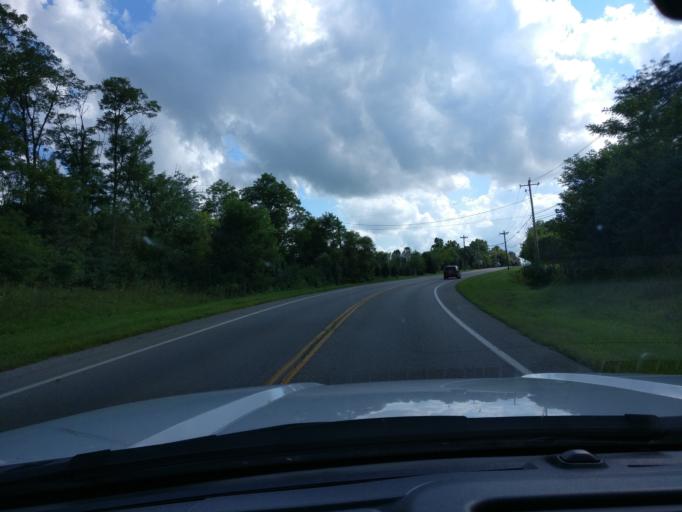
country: US
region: Ohio
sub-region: Warren County
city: Five Points
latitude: 39.5194
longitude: -84.1839
